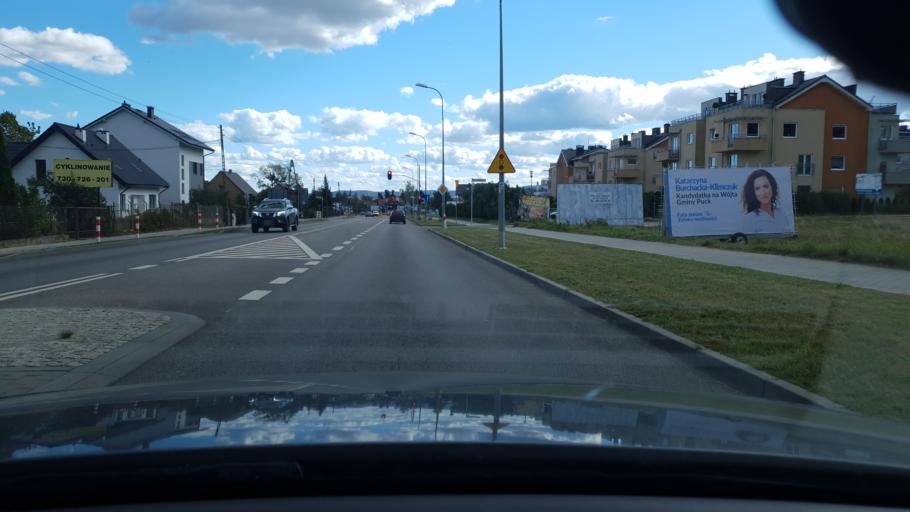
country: PL
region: Pomeranian Voivodeship
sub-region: Powiat wejherowski
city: Reda
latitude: 54.6183
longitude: 18.3428
